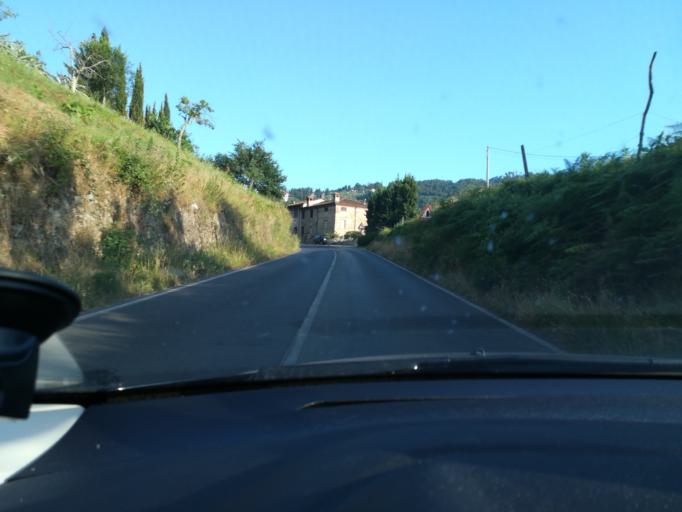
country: IT
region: Tuscany
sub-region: Provincia di Lucca
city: Stiava
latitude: 43.9189
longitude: 10.3342
